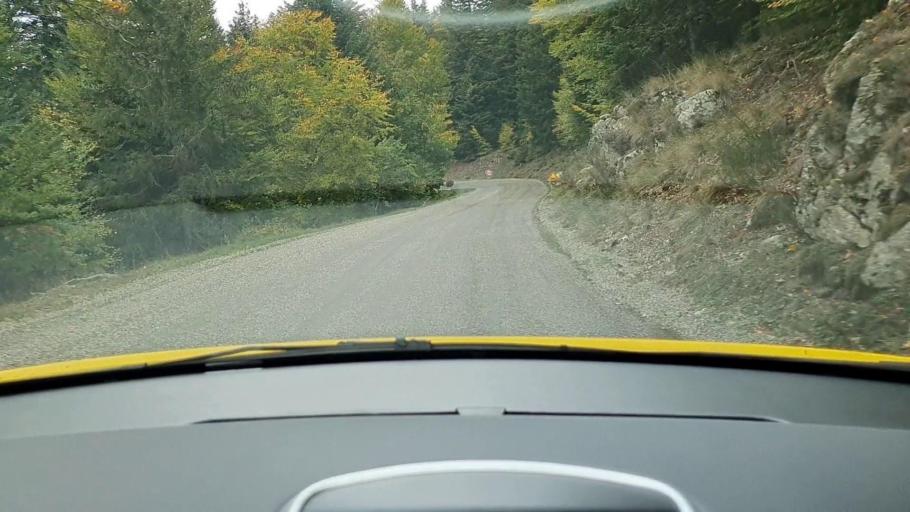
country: FR
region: Languedoc-Roussillon
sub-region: Departement du Gard
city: Le Vigan
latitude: 44.0620
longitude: 3.5460
